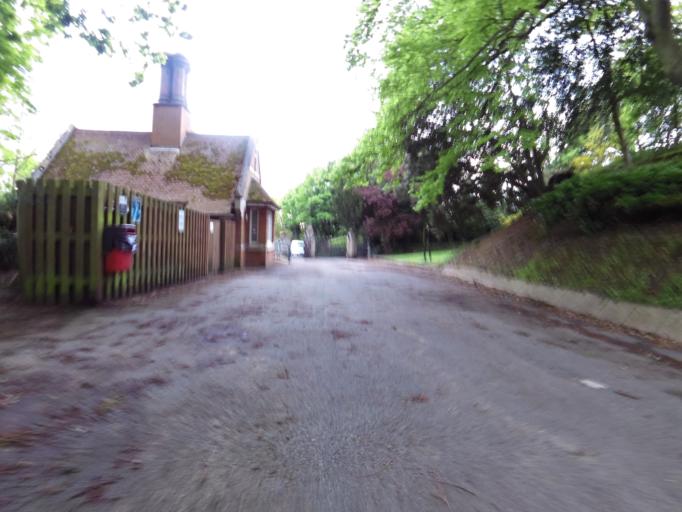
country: GB
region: England
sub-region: Suffolk
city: Ipswich
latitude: 52.0629
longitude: 1.1676
